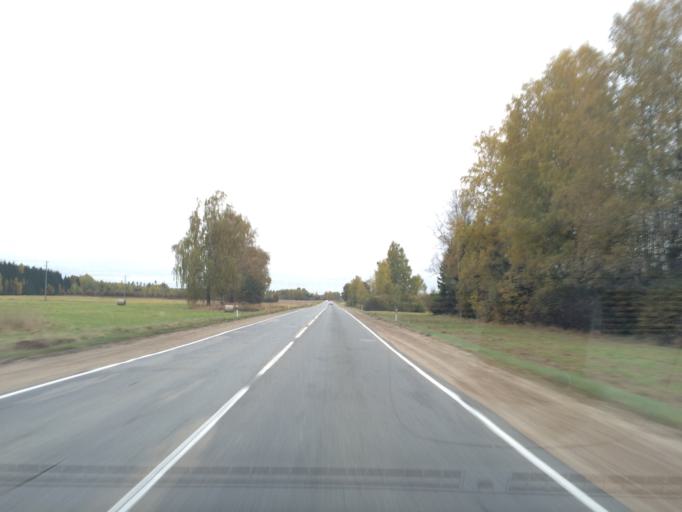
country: LV
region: Plavinu
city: Plavinas
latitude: 56.5989
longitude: 25.7822
